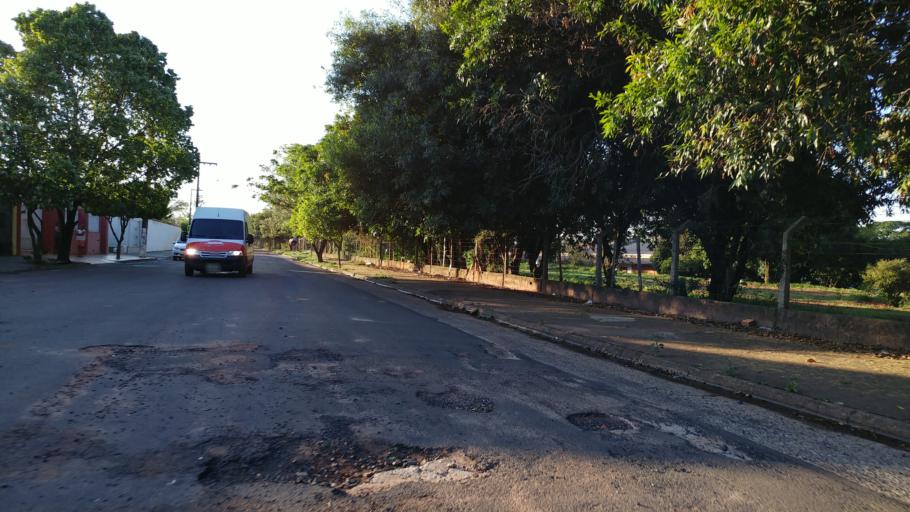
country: BR
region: Sao Paulo
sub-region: Paraguacu Paulista
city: Paraguacu Paulista
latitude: -22.4054
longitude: -50.5765
